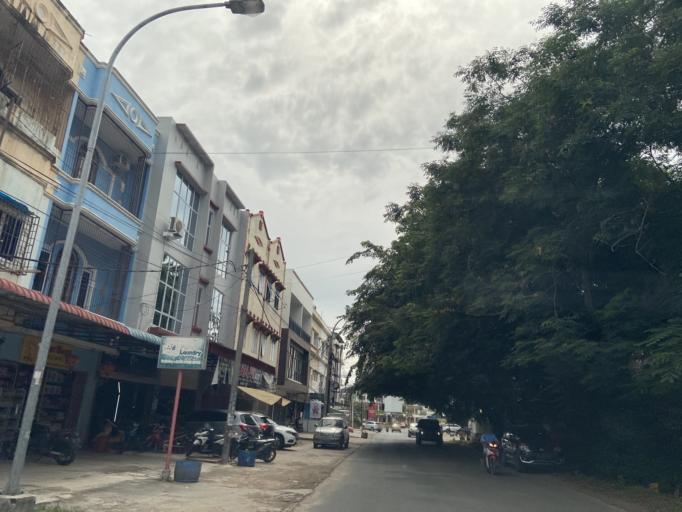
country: SG
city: Singapore
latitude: 1.1413
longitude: 104.0084
